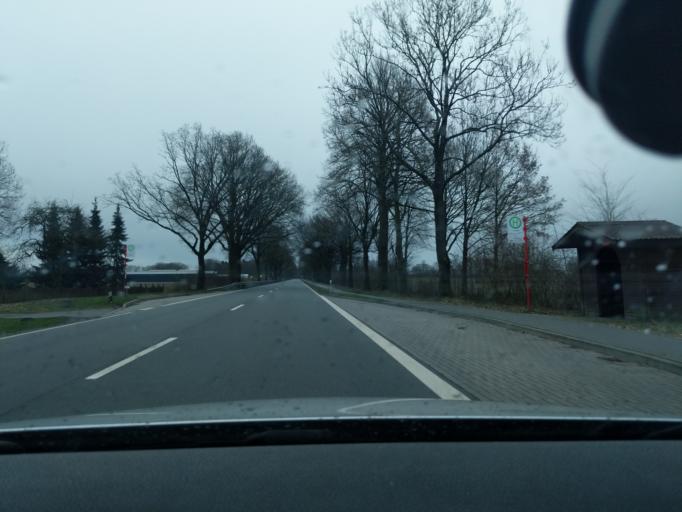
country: DE
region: Lower Saxony
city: Heinbockel
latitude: 53.5436
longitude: 9.3091
